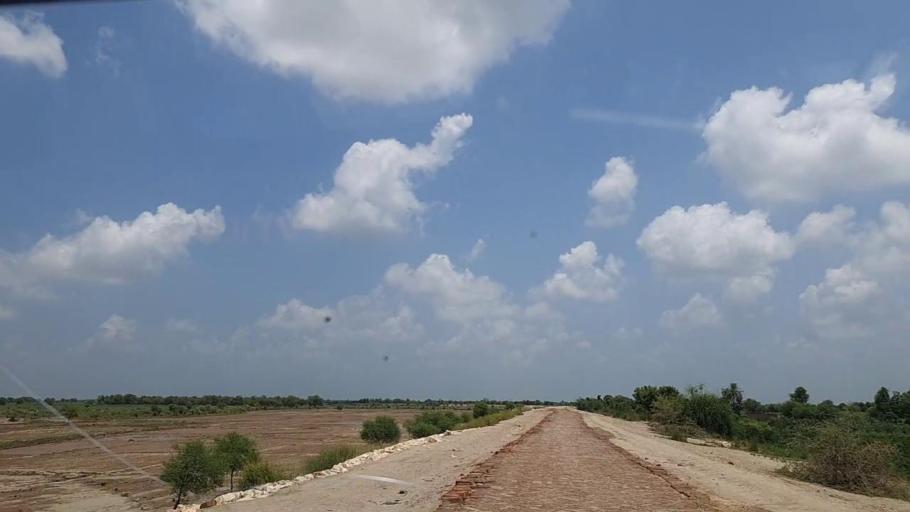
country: PK
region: Sindh
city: Tharu Shah
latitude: 26.9370
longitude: 68.0015
